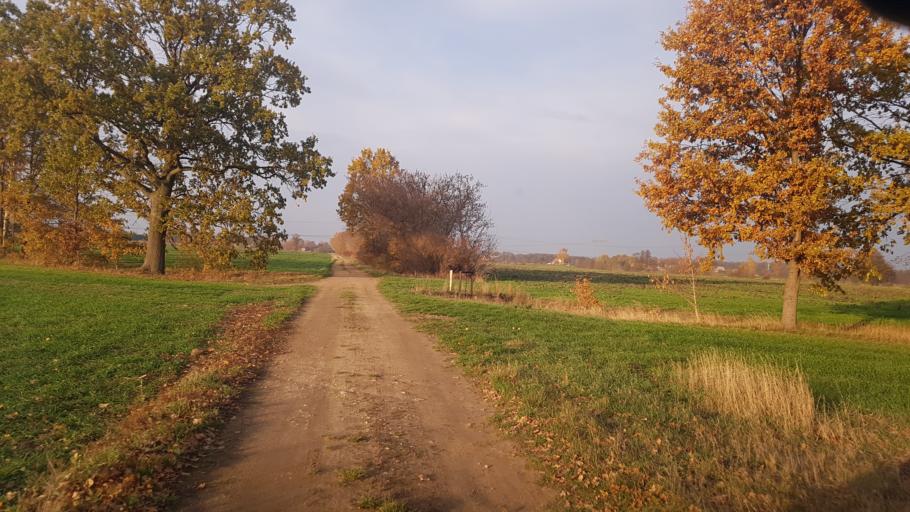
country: DE
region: Brandenburg
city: Schonewalde
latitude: 51.6482
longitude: 13.5994
